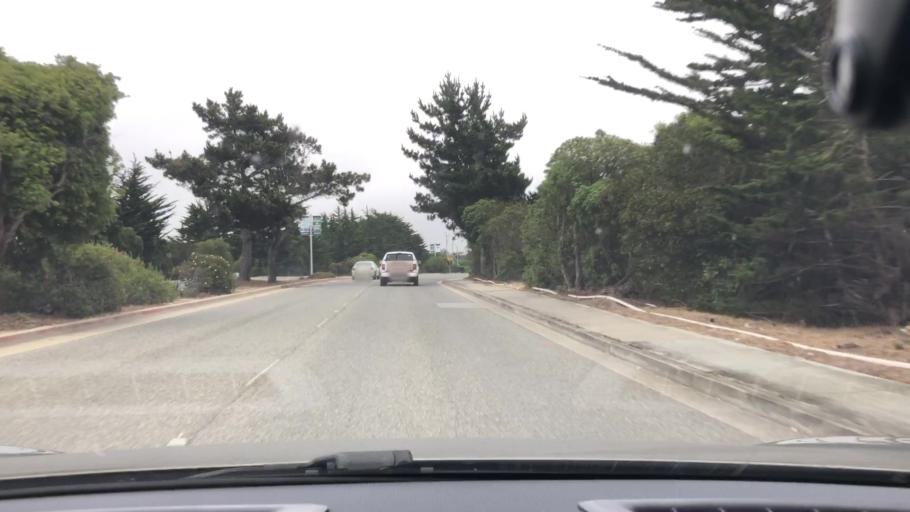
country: US
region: California
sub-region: Monterey County
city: Marina
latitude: 36.6480
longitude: -121.8074
